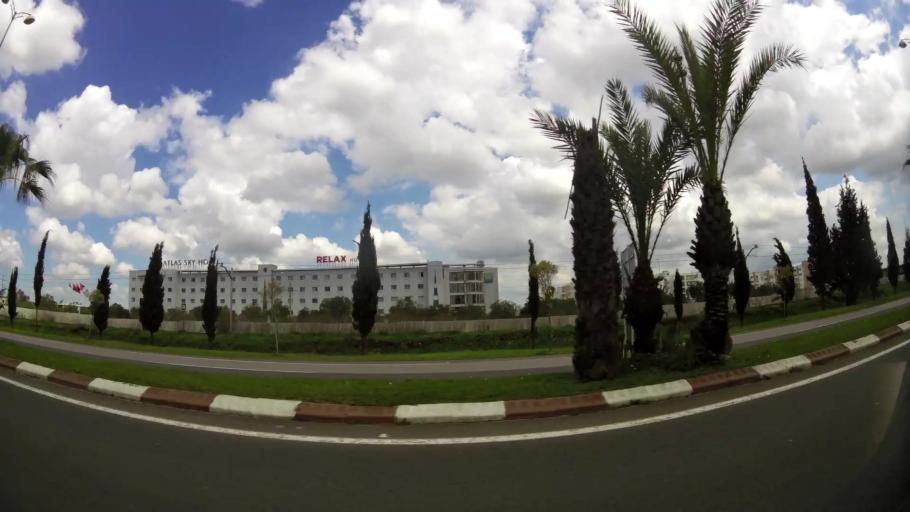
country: MA
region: Chaouia-Ouardigha
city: Nouaseur
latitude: 33.3927
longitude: -7.5673
